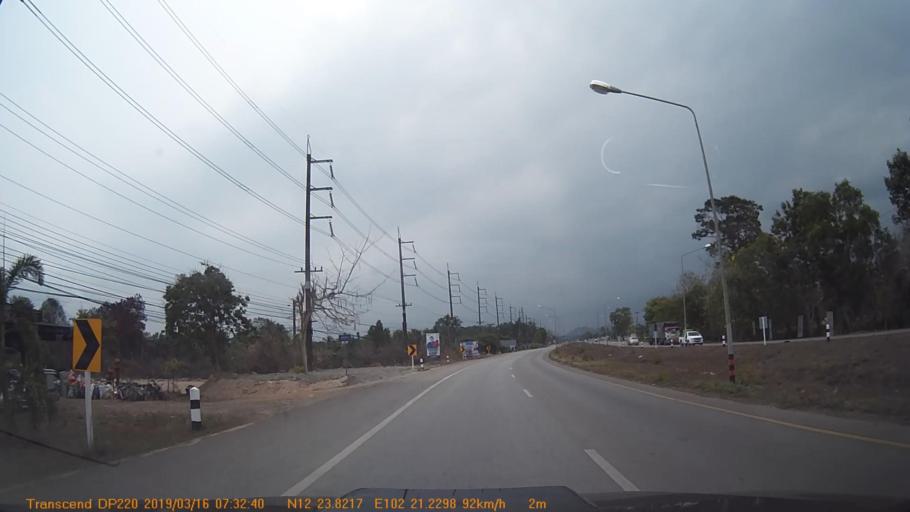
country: TH
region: Trat
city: Khao Saming
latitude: 12.3911
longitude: 102.3666
